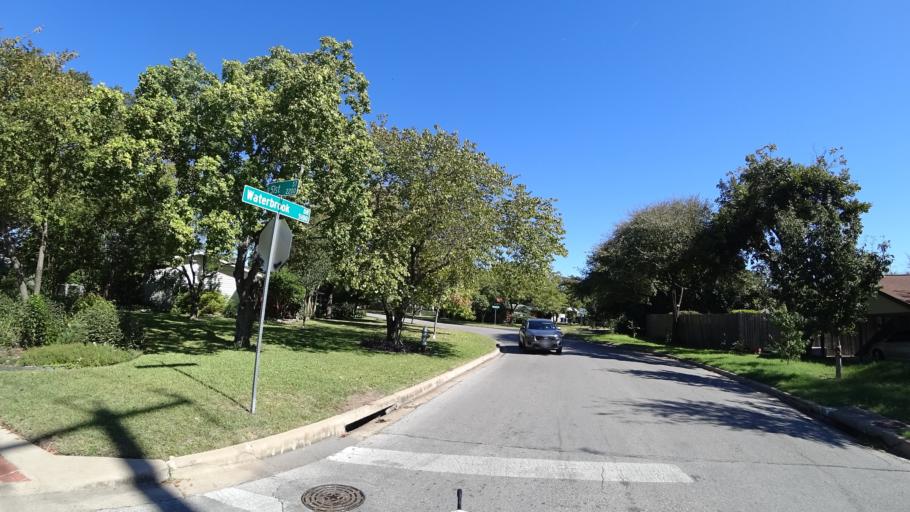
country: US
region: Texas
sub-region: Travis County
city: Austin
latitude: 30.3010
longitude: -97.6902
